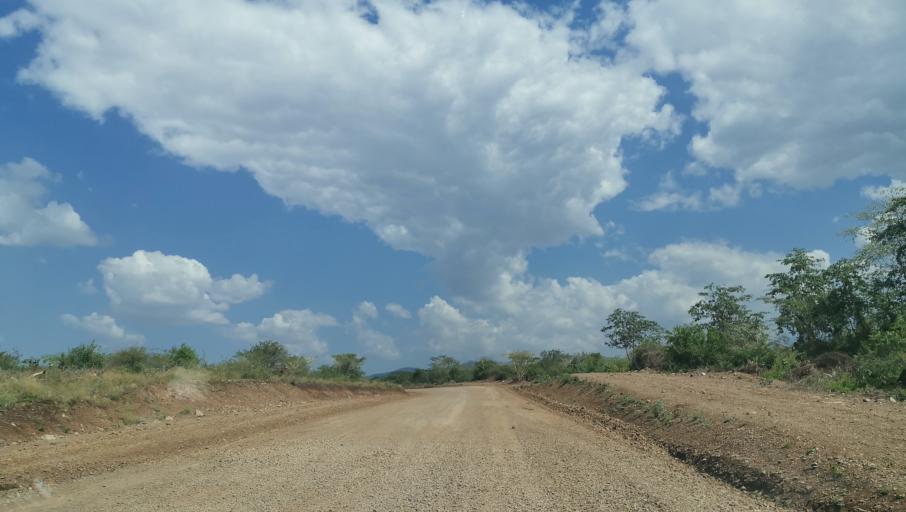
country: ET
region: Southern Nations, Nationalities, and People's Region
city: Felege Neway
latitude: 6.3625
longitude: 37.2834
